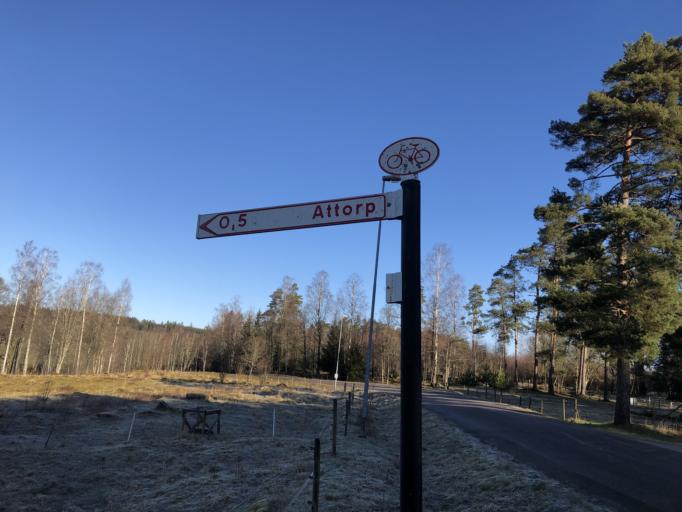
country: SE
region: Vaestra Goetaland
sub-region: Ulricehamns Kommun
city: Ulricehamn
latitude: 57.6902
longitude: 13.4184
